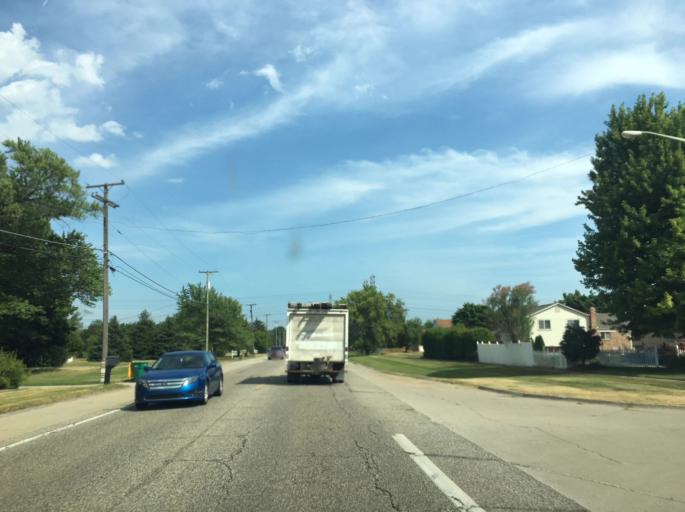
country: US
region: Michigan
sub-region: Macomb County
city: Sterling Heights
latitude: 42.5856
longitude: -83.0017
